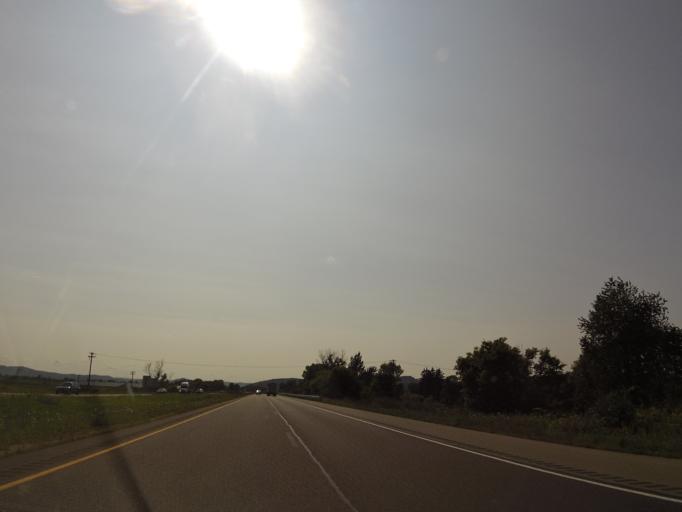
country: US
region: Wisconsin
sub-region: La Crosse County
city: West Salem
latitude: 43.8904
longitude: -91.0971
